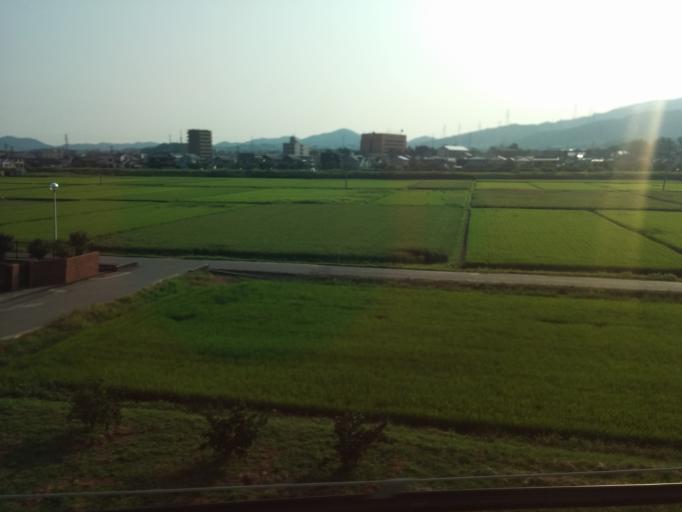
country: JP
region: Aichi
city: Gamagori
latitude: 34.8618
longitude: 137.1592
